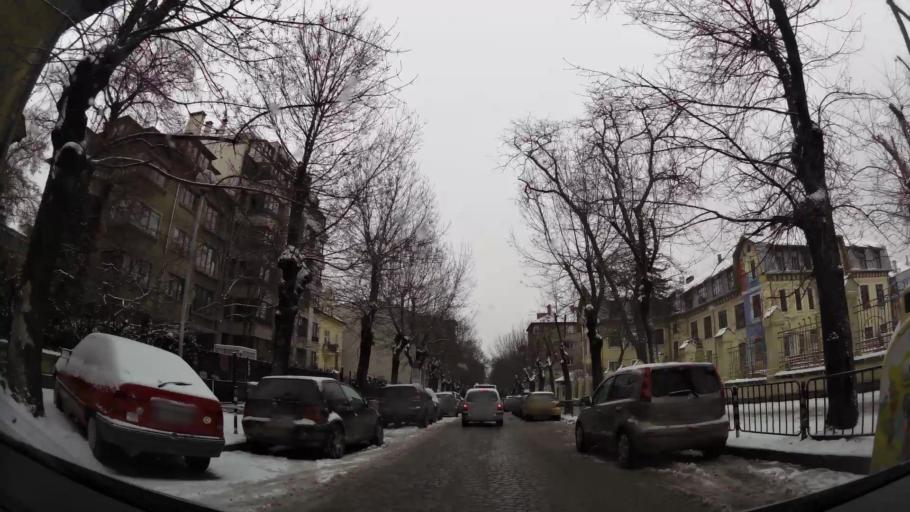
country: BG
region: Sofia-Capital
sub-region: Stolichna Obshtina
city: Sofia
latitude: 42.6931
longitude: 23.3417
